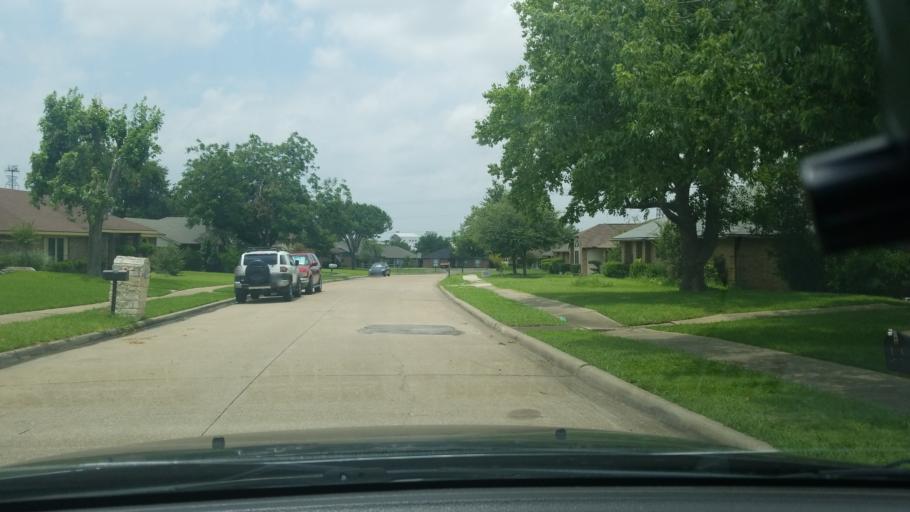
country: US
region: Texas
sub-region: Dallas County
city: Mesquite
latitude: 32.8024
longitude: -96.6203
